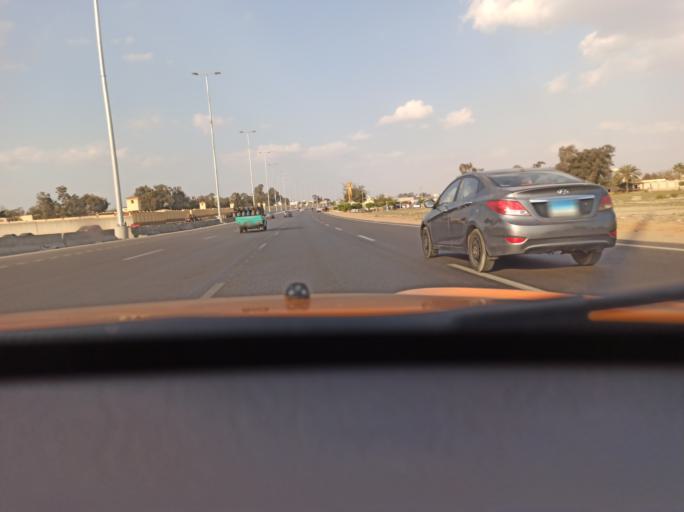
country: EG
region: Al Isma'iliyah
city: Ismailia
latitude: 30.6121
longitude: 32.2201
